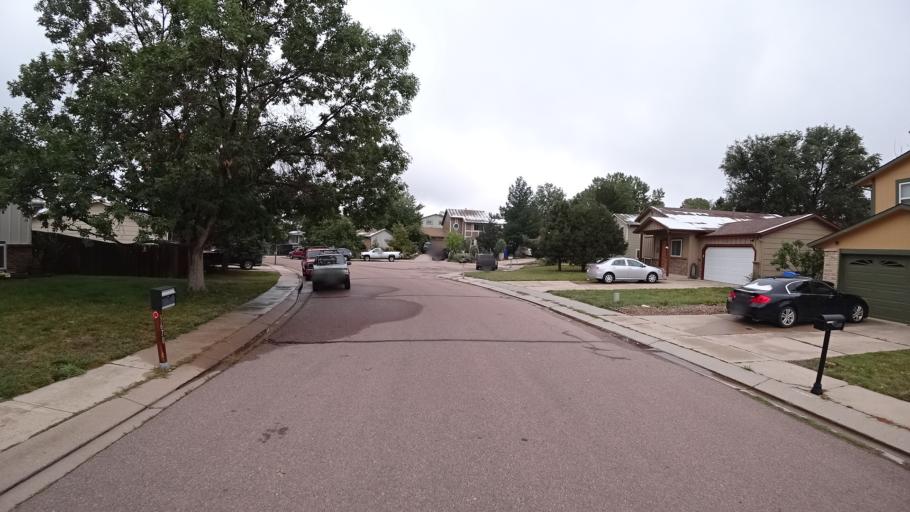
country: US
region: Colorado
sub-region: El Paso County
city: Cimarron Hills
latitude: 38.9170
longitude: -104.7581
